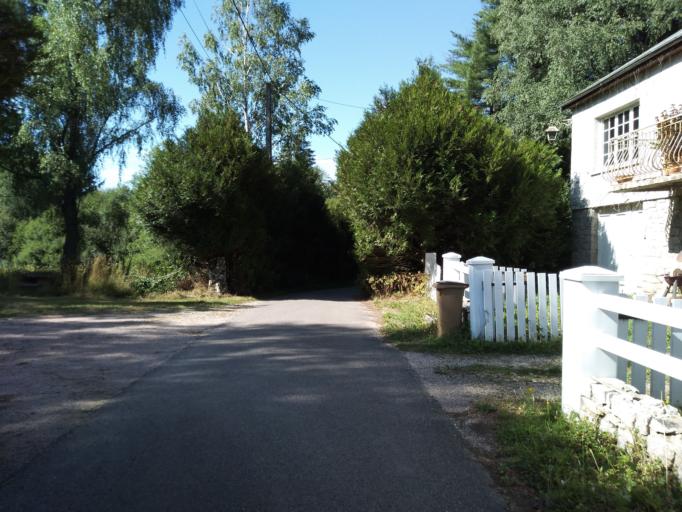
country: FR
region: Bourgogne
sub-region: Departement de la Cote-d'Or
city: Saulieu
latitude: 47.2925
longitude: 4.1373
